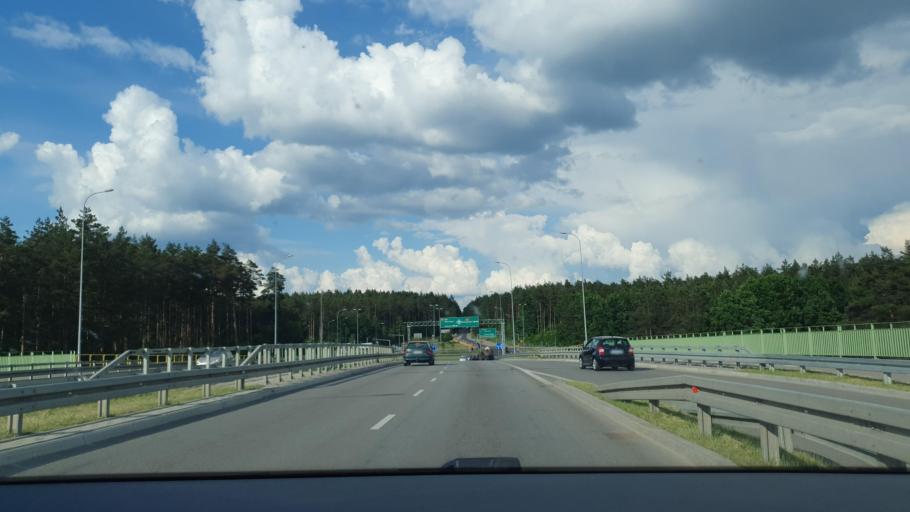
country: PL
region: Podlasie
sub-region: Bialystok
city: Bialystok
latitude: 53.1278
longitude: 23.2201
